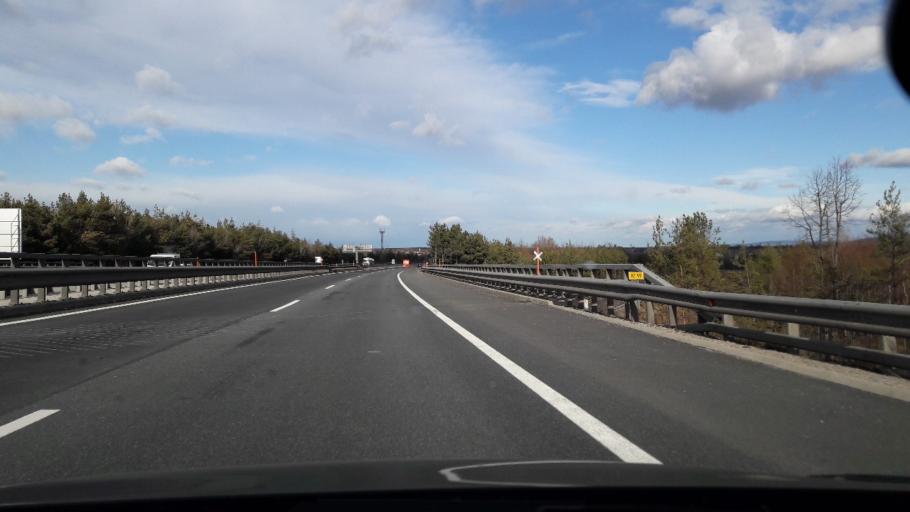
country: AT
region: Lower Austria
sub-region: Politischer Bezirk Neunkirchen
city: Breitenau
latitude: 47.7144
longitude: 16.1316
